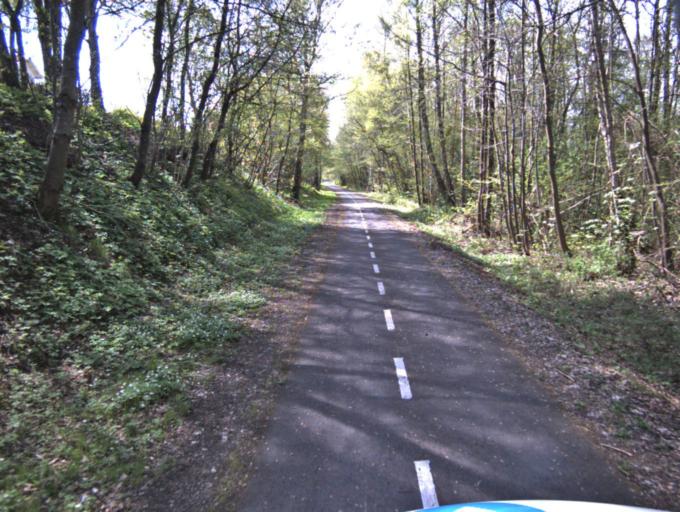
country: SE
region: Skane
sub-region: Kristianstads Kommun
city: Onnestad
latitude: 55.9981
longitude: 14.0404
